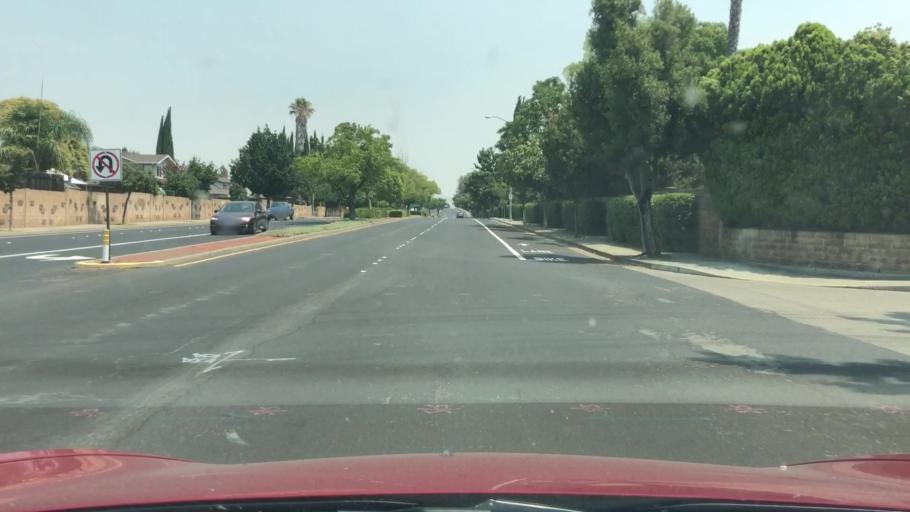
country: US
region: California
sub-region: Alameda County
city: Livermore
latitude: 37.6607
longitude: -121.7894
